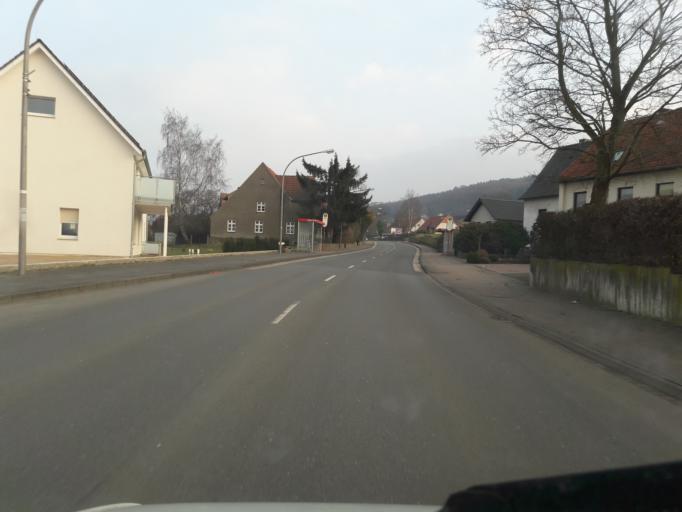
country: DE
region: North Rhine-Westphalia
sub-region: Regierungsbezirk Detmold
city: Huellhorst
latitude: 52.3048
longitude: 8.6908
